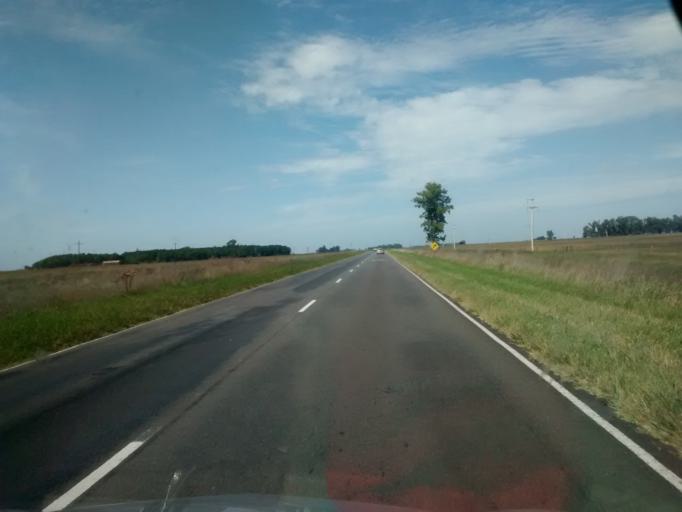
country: AR
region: Buenos Aires
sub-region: Partido de Ayacucho
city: Ayacucho
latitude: -36.9103
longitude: -58.5261
